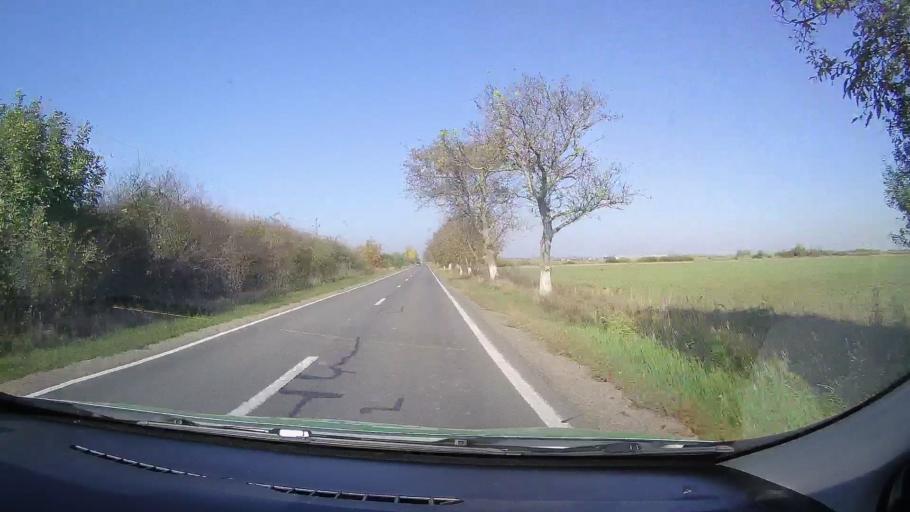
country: RO
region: Satu Mare
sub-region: Comuna Urziceni
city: Urziceni
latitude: 47.7134
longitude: 22.4244
